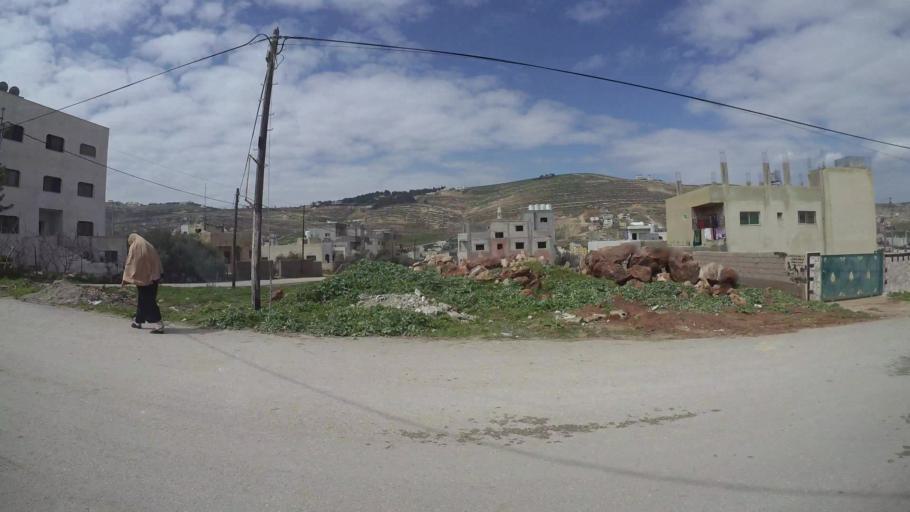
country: JO
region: Amman
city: Al Jubayhah
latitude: 32.0616
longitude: 35.8149
